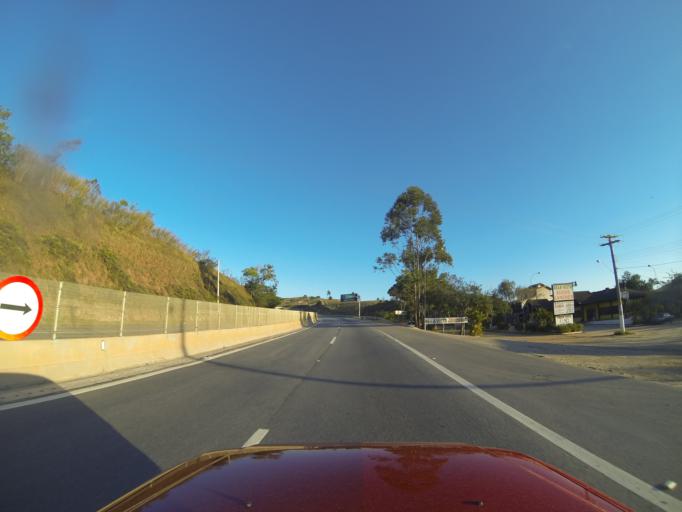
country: BR
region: Sao Paulo
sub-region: Santa Branca
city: Santa Branca
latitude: -23.4182
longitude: -45.6391
